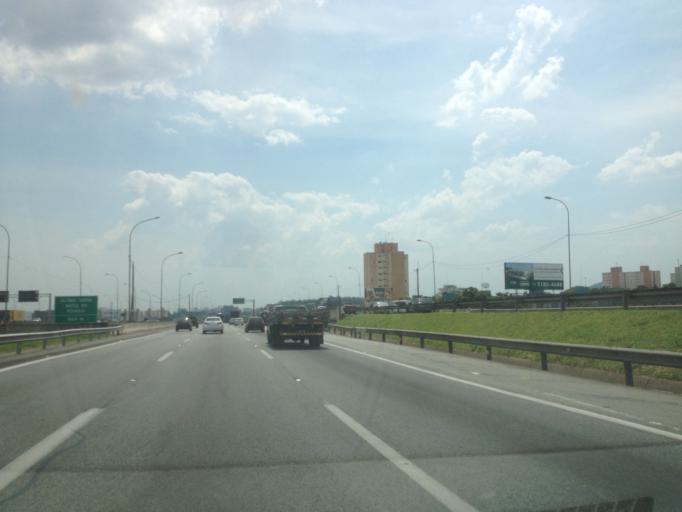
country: BR
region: Sao Paulo
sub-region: Osasco
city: Osasco
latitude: -23.5178
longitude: -46.7875
